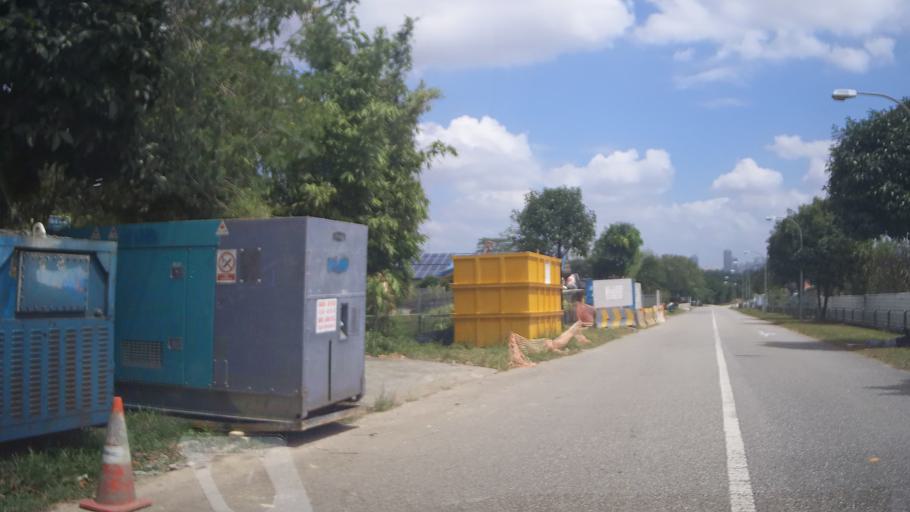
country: MY
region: Johor
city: Johor Bahru
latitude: 1.4382
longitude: 103.7262
